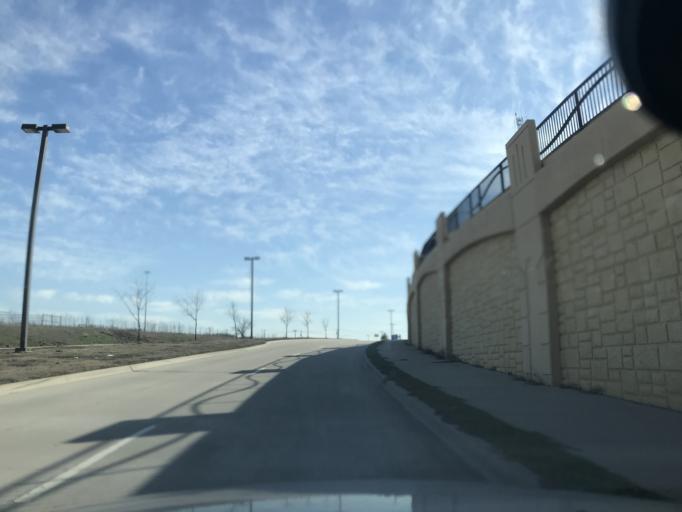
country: US
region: Texas
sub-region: Denton County
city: The Colony
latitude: 33.0857
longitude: -96.8540
